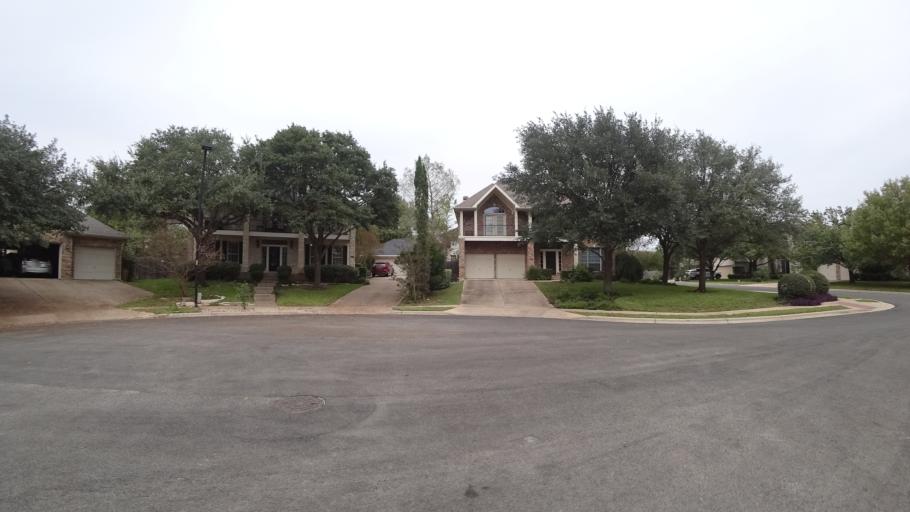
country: US
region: Texas
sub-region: Travis County
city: Shady Hollow
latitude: 30.1848
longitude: -97.8885
